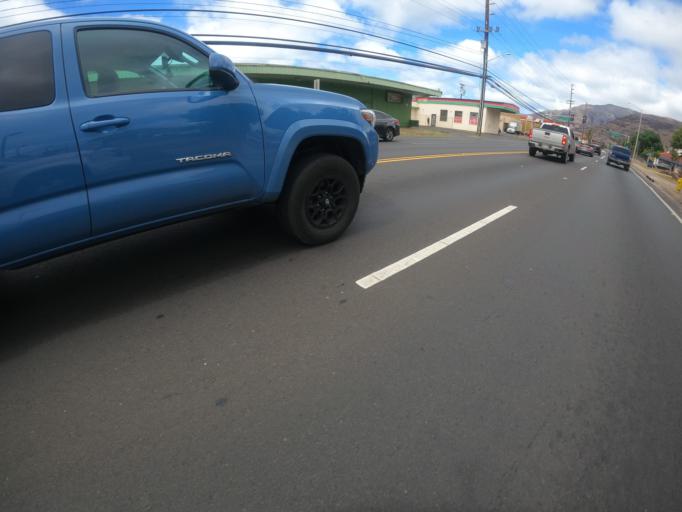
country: US
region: Hawaii
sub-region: Honolulu County
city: Waianae
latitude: 21.4409
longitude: -158.1866
